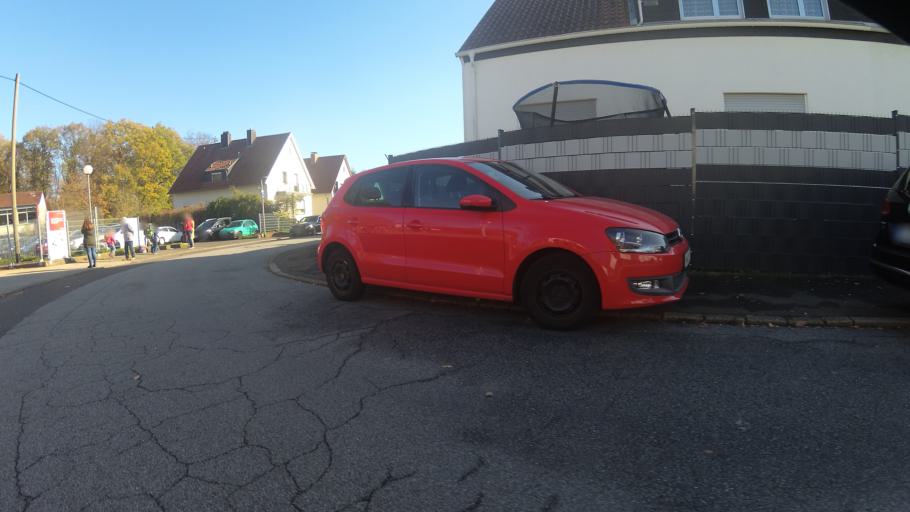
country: DE
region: Saarland
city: Neunkirchen
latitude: 49.3456
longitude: 7.2000
